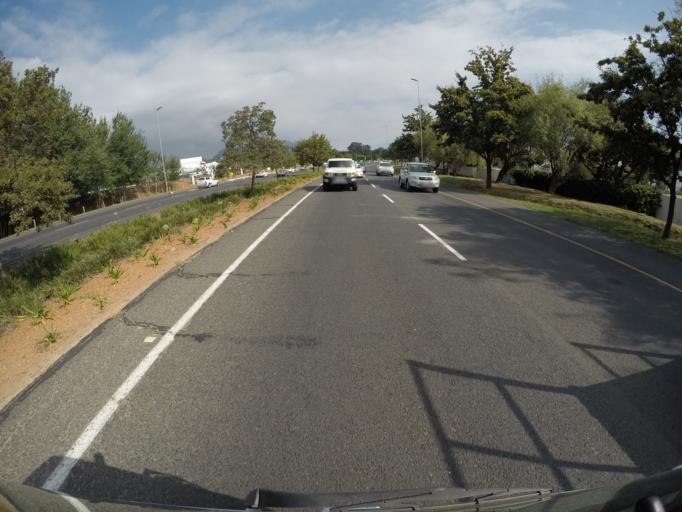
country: ZA
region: Western Cape
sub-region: Cape Winelands District Municipality
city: Stellenbosch
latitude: -33.9536
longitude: 18.8558
